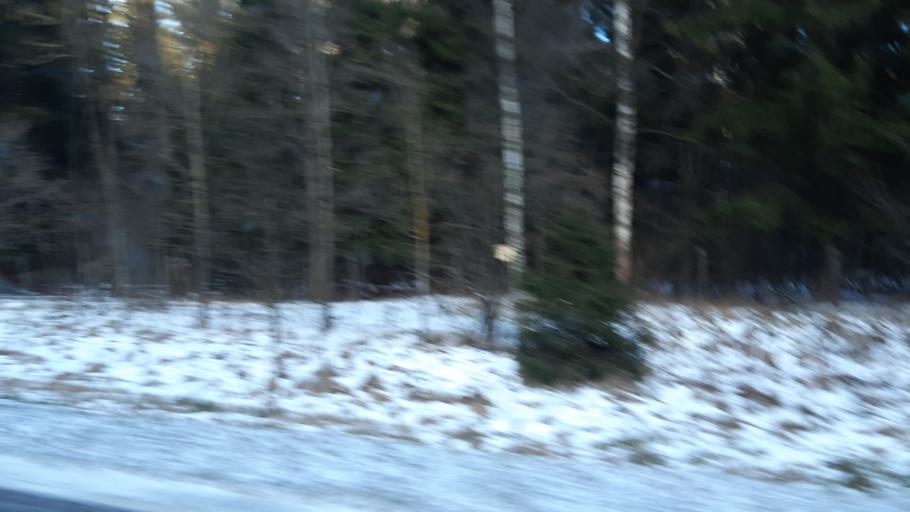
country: RU
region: Vladimir
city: Arsaki
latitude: 56.2643
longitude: 38.4309
